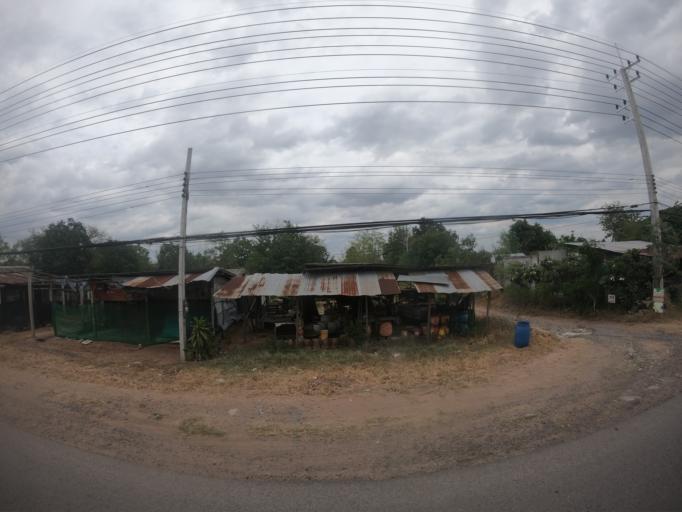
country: TH
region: Nakhon Ratchasima
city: Chok Chai
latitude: 14.8241
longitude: 102.1806
